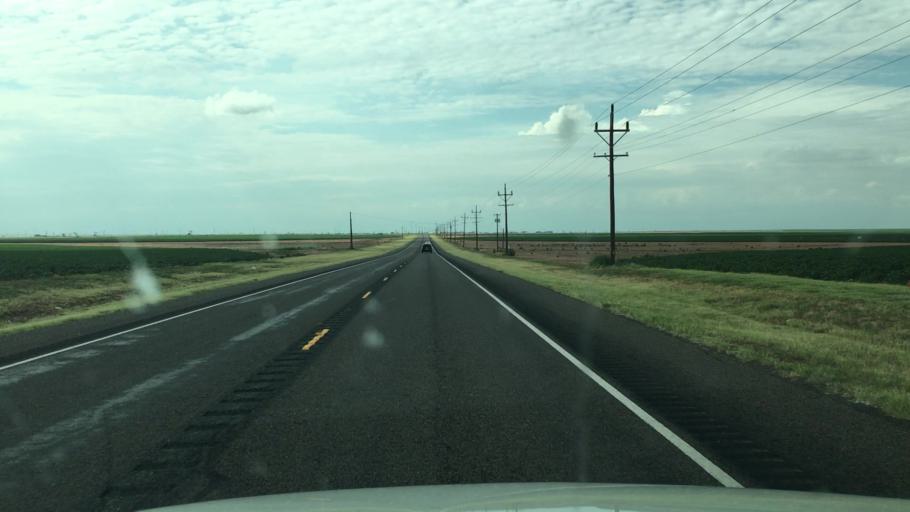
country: US
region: Texas
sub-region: Dawson County
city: Lamesa
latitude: 32.8818
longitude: -102.0816
